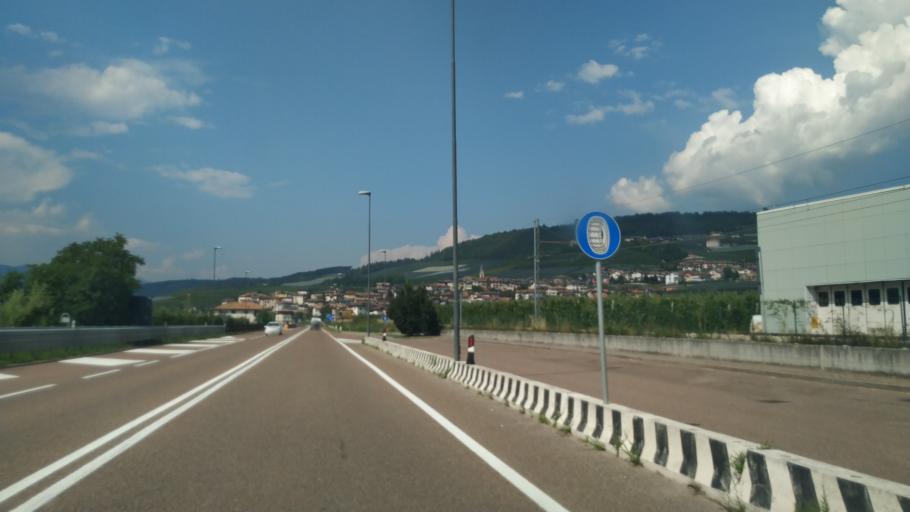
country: IT
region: Trentino-Alto Adige
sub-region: Provincia di Trento
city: Taio
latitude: 46.2996
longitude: 11.0697
